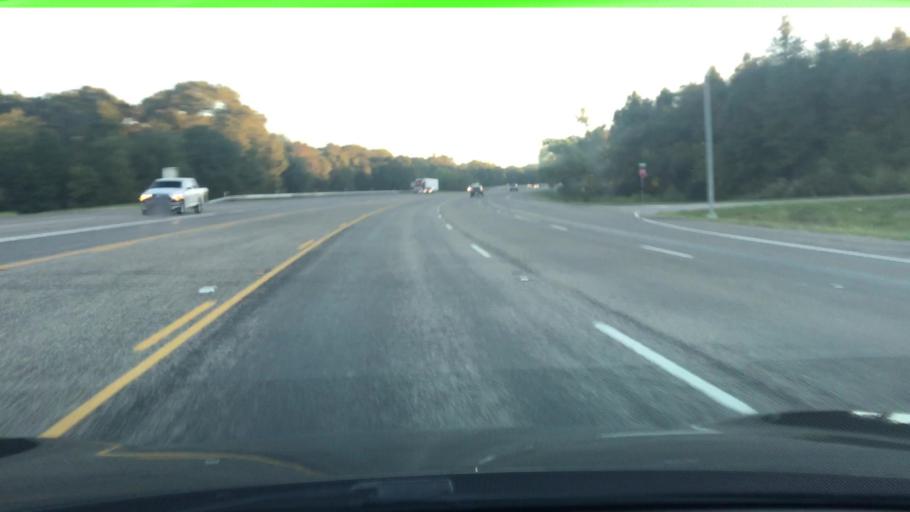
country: US
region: Texas
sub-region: Henderson County
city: Athens
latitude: 32.1931
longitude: -95.8113
